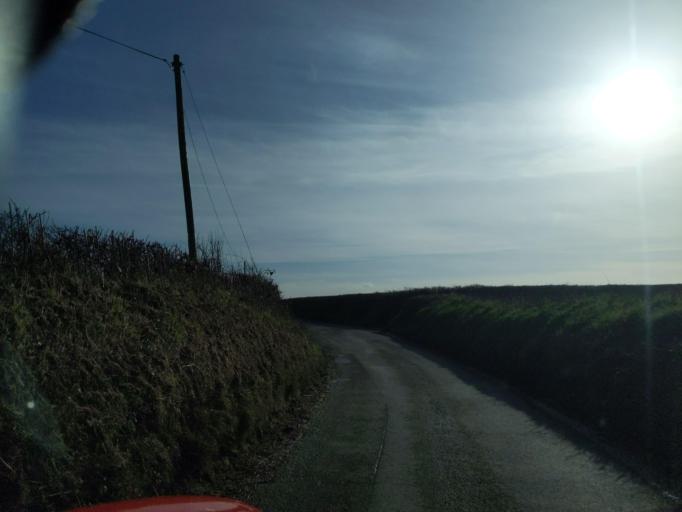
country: GB
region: England
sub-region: Devon
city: Kingsbridge
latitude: 50.3363
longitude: -3.7209
